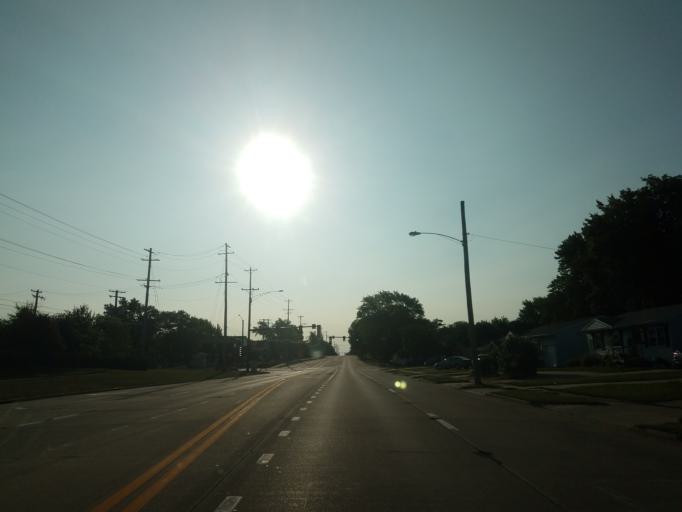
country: US
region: Illinois
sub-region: McLean County
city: Normal
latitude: 40.5316
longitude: -88.9903
